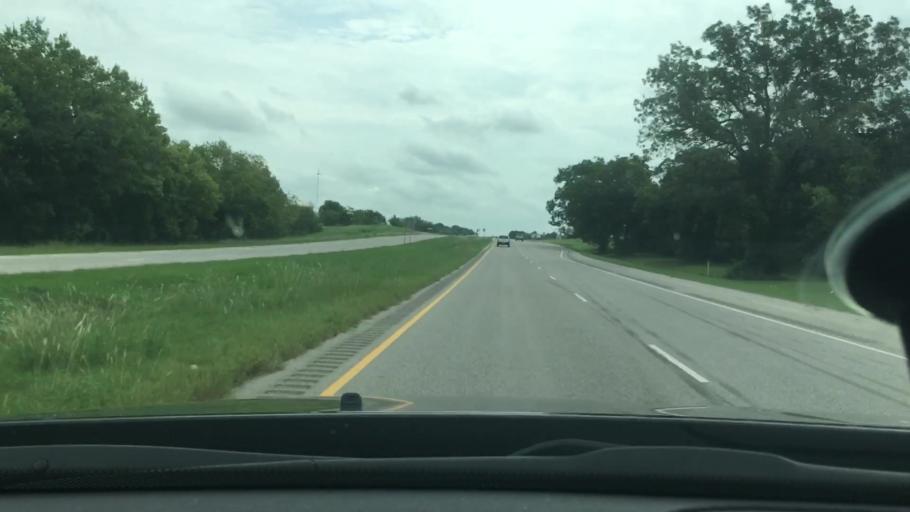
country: US
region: Oklahoma
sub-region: Carter County
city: Wilson
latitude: 34.1729
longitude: -97.4201
